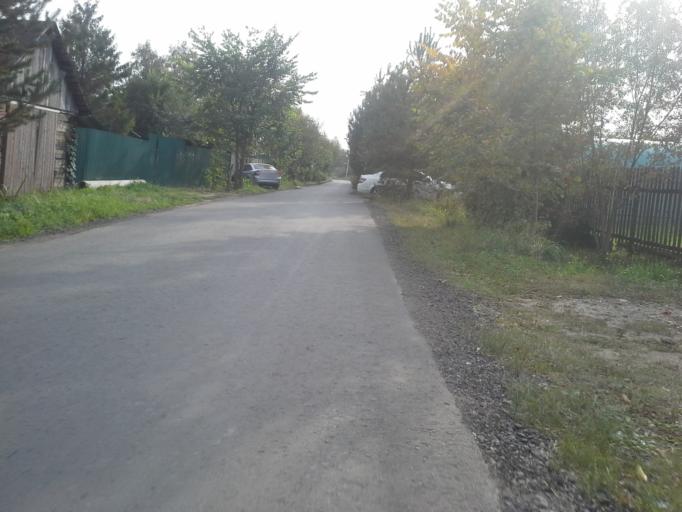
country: RU
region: Moskovskaya
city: Aprelevka
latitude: 55.5599
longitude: 37.0628
